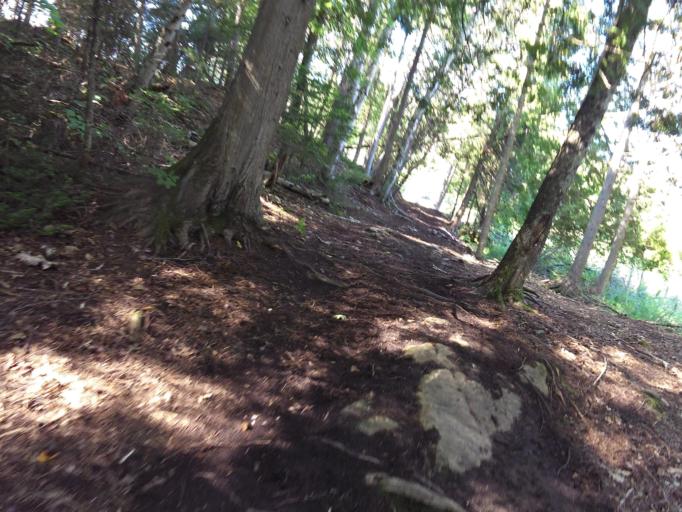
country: CA
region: Ontario
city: Renfrew
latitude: 45.1323
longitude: -76.7302
